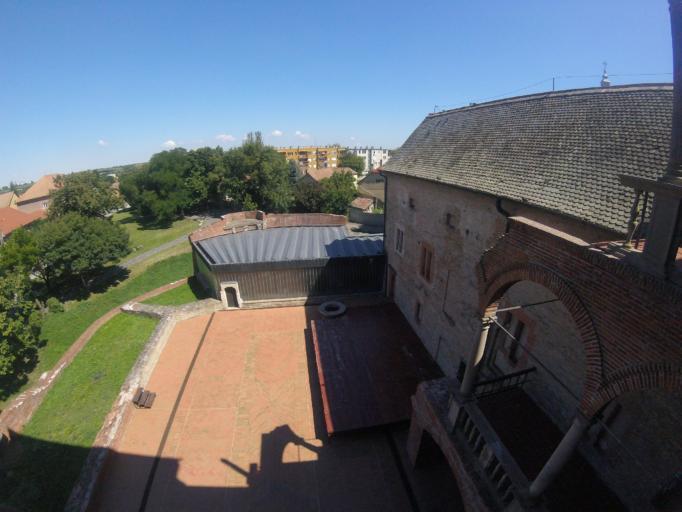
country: HU
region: Tolna
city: Simontornya
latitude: 46.7523
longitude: 18.5526
